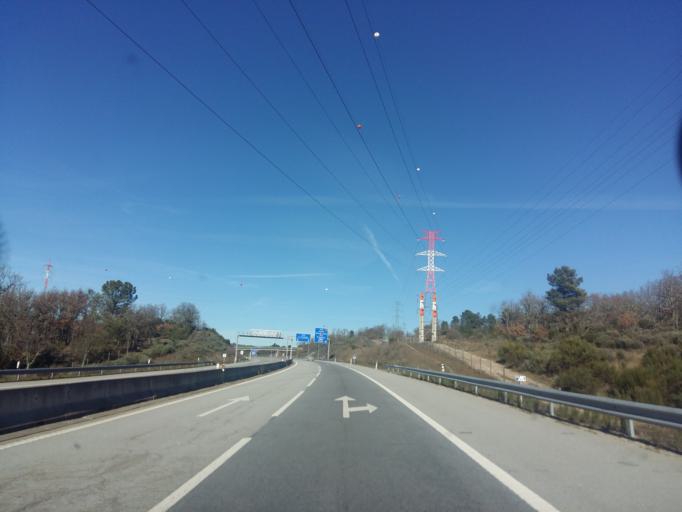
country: PT
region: Guarda
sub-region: Guarda
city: Sequeira
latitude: 40.5565
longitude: -7.2166
